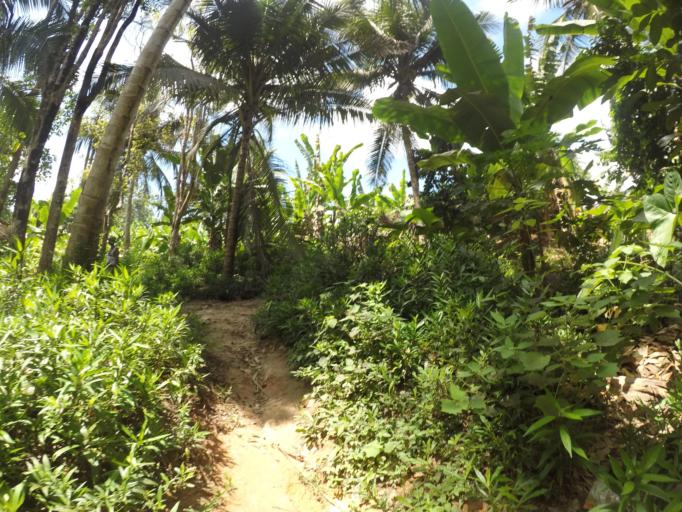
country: TZ
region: Pemba South
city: Mtambile
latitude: -5.3811
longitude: 39.7141
